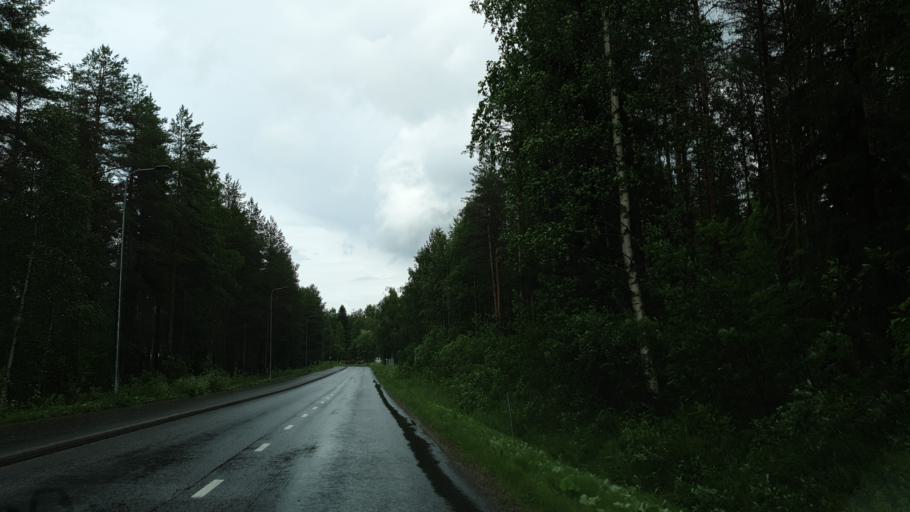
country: FI
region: Kainuu
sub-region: Kehys-Kainuu
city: Kuhmo
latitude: 64.1220
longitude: 29.4995
